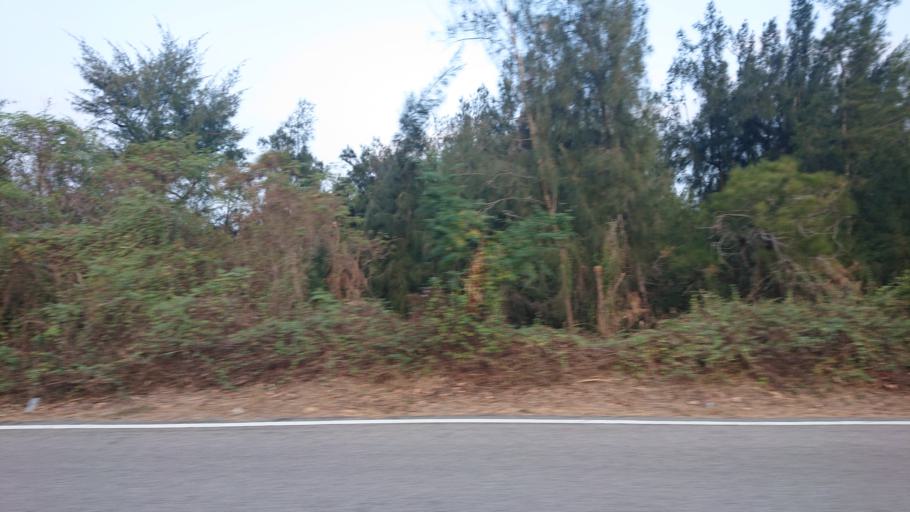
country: CN
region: Fujian
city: Shijing
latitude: 24.4943
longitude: 118.4452
